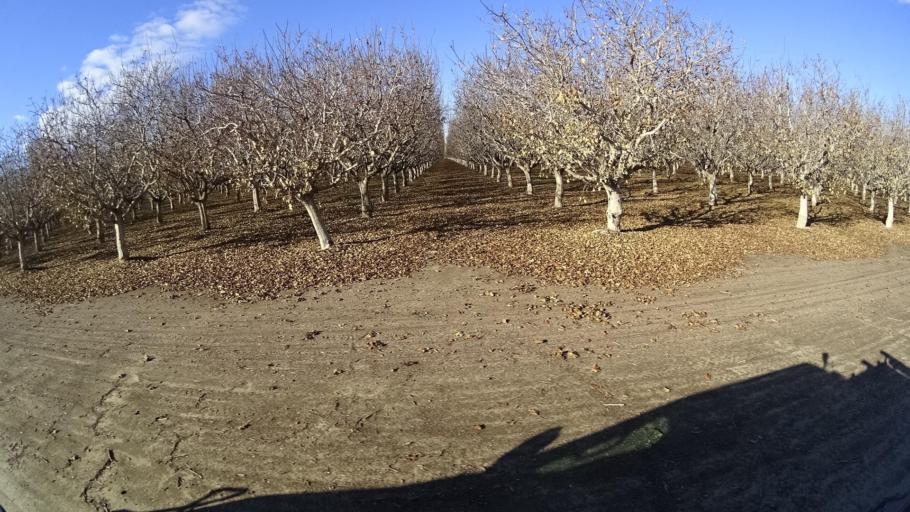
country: US
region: California
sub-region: Kern County
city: McFarland
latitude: 35.6947
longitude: -119.2942
